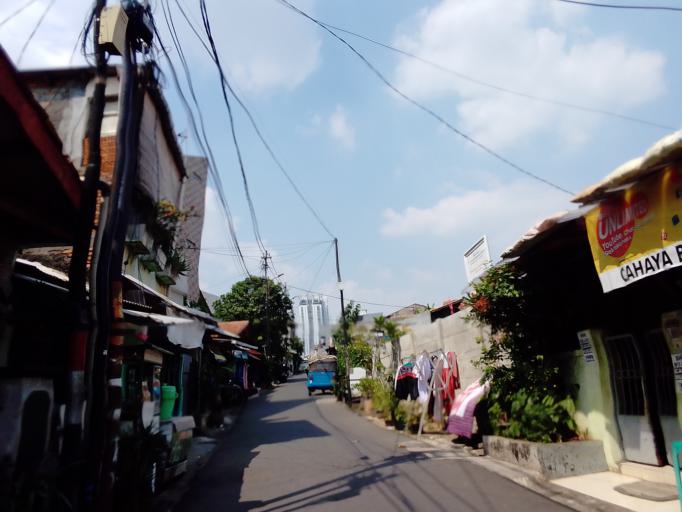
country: ID
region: Jakarta Raya
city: Jakarta
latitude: -6.2588
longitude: 106.7982
